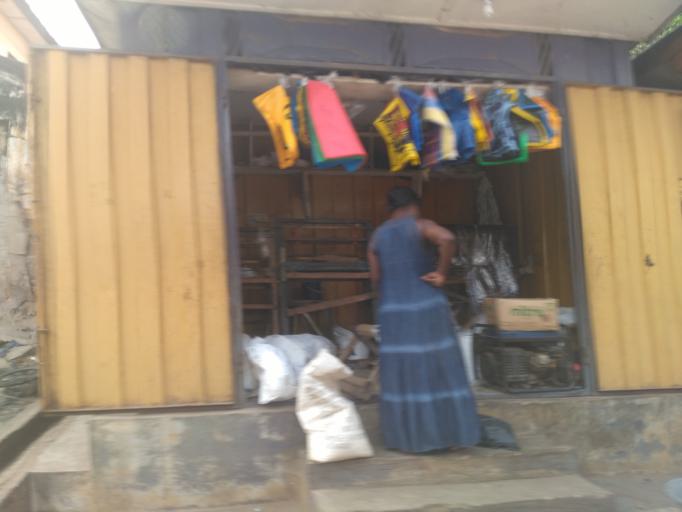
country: GH
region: Ashanti
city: Kumasi
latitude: 6.6953
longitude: -1.6107
